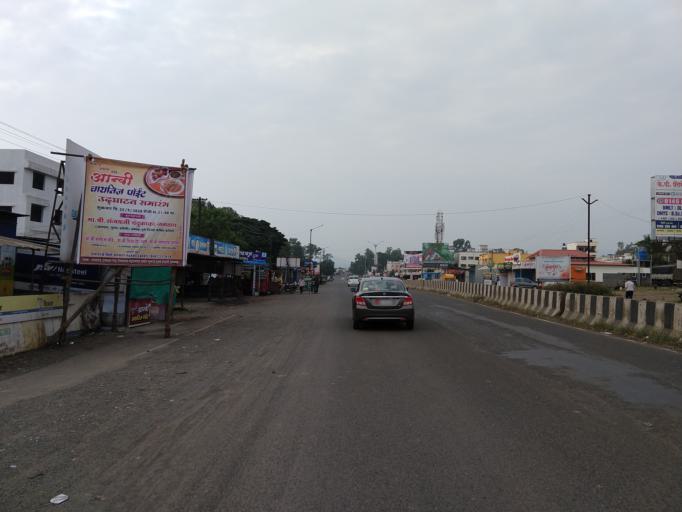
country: IN
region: Maharashtra
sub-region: Pune Division
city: Sasvad
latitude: 18.3531
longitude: 74.0287
